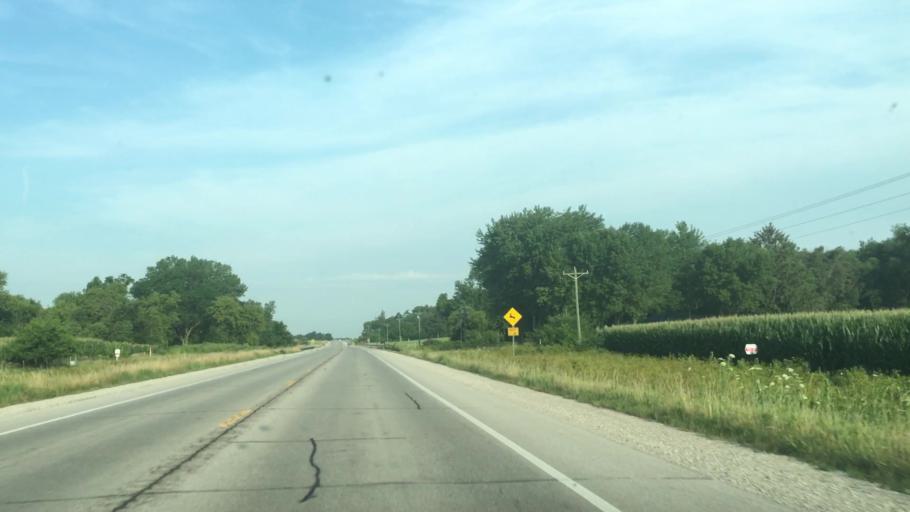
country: US
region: Iowa
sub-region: Johnson County
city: Tiffin
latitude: 41.7141
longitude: -91.7090
